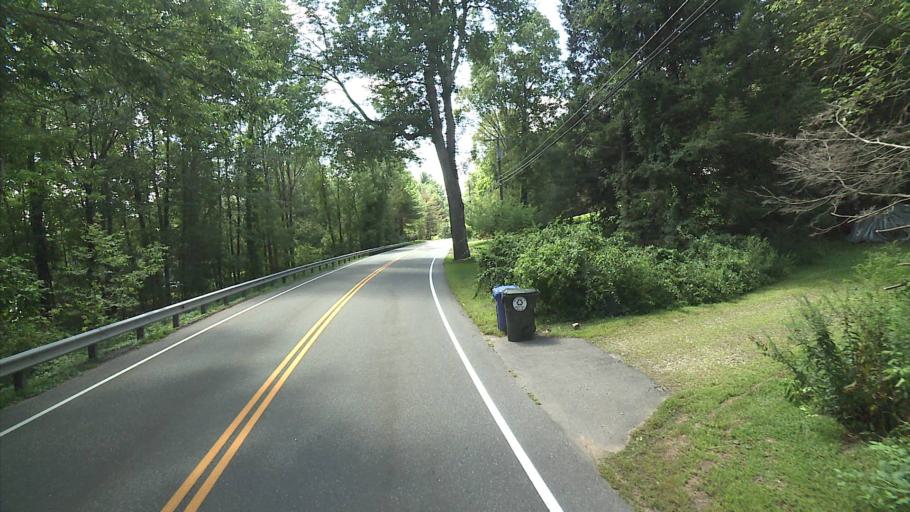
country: US
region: Connecticut
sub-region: Windham County
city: South Woodstock
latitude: 41.9516
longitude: -72.0756
